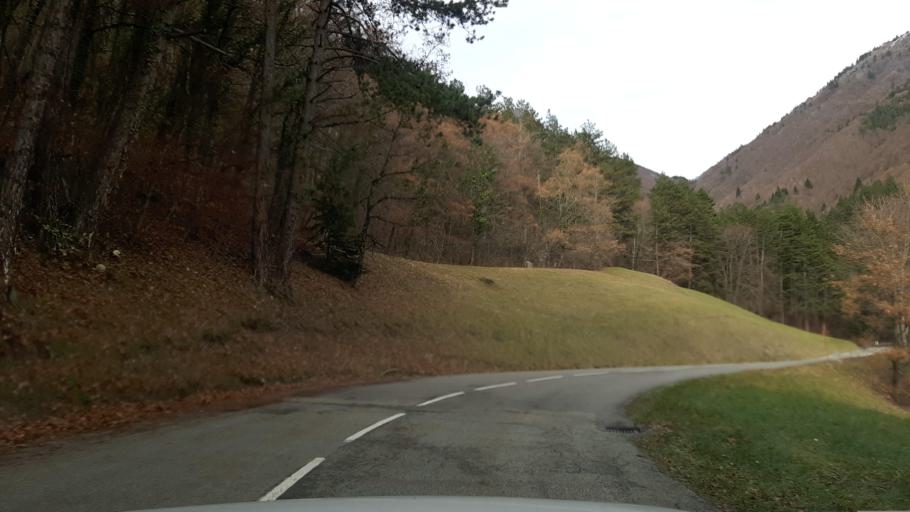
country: FR
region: Rhone-Alpes
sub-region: Departement de la Savoie
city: Coise-Saint-Jean-Pied-Gauthier
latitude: 45.5851
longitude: 6.1525
